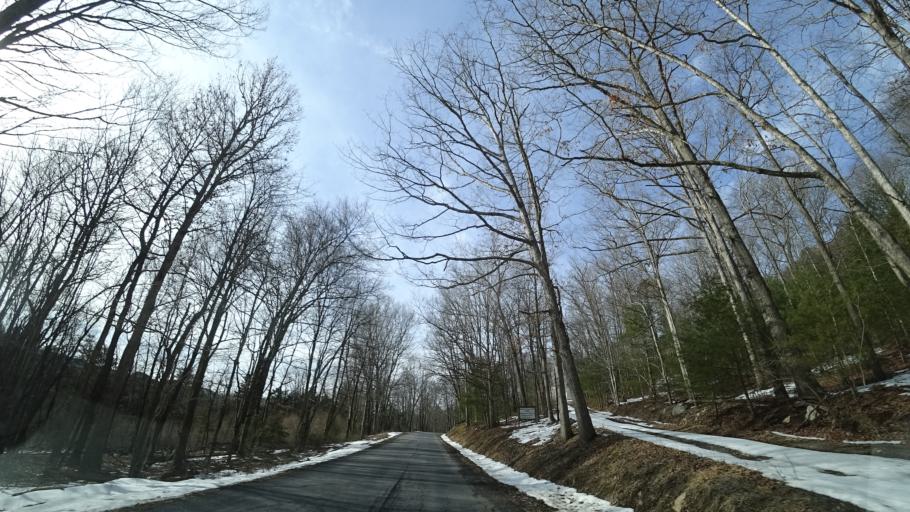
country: US
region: Virginia
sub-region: Shenandoah County
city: Edinburg
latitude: 38.9583
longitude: -78.6836
